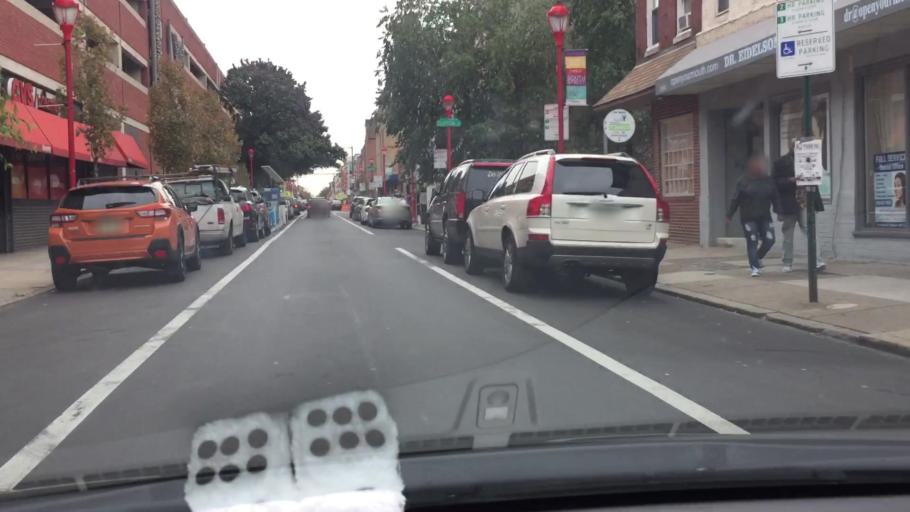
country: US
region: Pennsylvania
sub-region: Philadelphia County
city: Philadelphia
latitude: 39.9430
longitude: -75.1601
